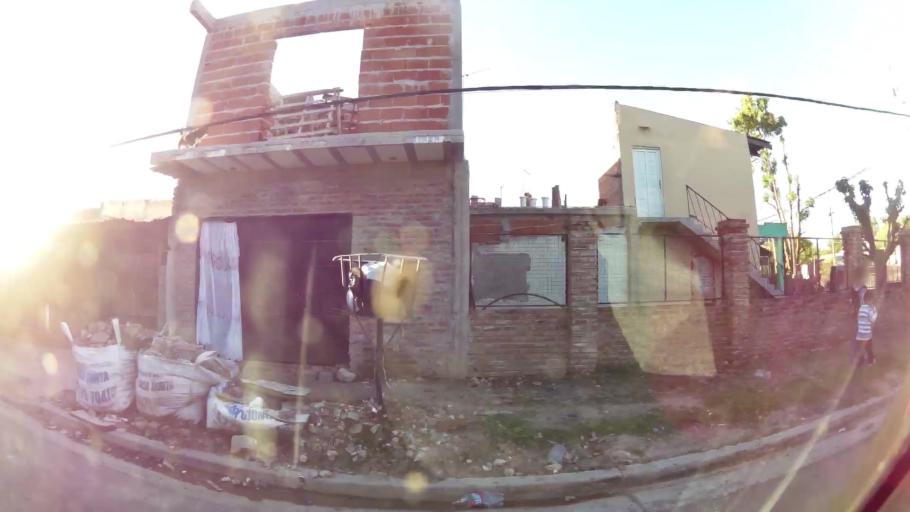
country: AR
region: Buenos Aires
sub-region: Partido de Almirante Brown
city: Adrogue
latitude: -34.7726
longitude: -58.3408
